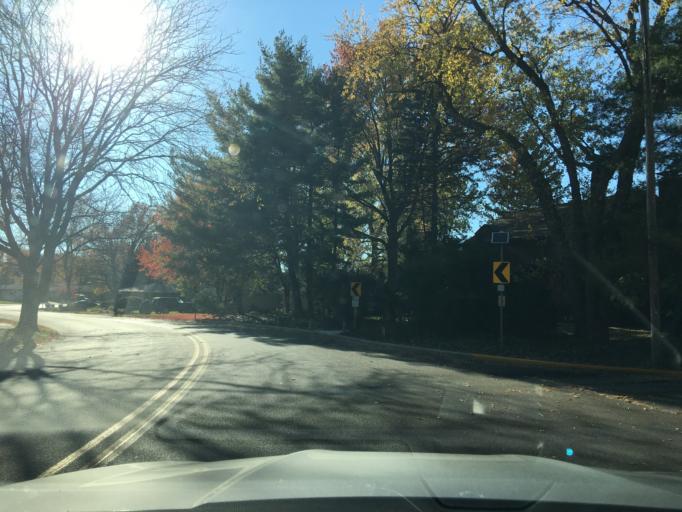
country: US
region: Indiana
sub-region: Tippecanoe County
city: West Lafayette
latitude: 40.4352
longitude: -86.9087
